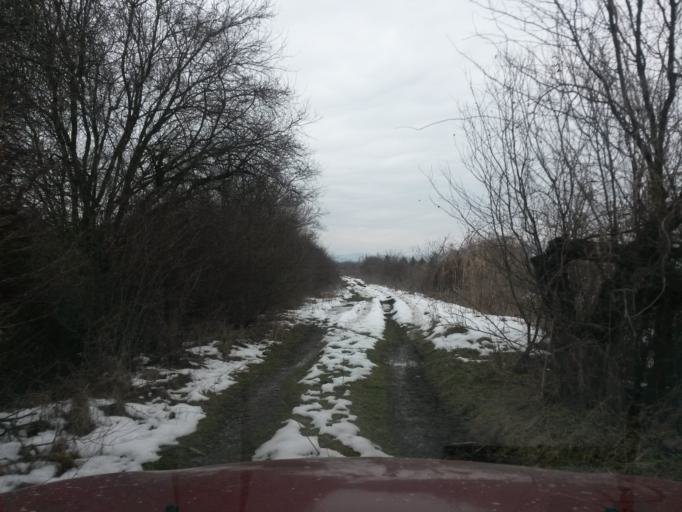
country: SK
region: Kosicky
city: Vinne
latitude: 48.7425
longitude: 22.0244
